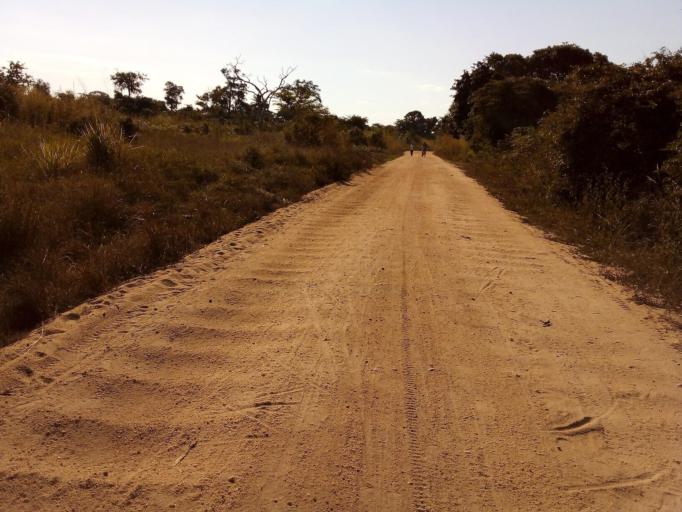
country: MZ
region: Zambezia
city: Quelimane
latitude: -17.5483
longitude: 36.6286
